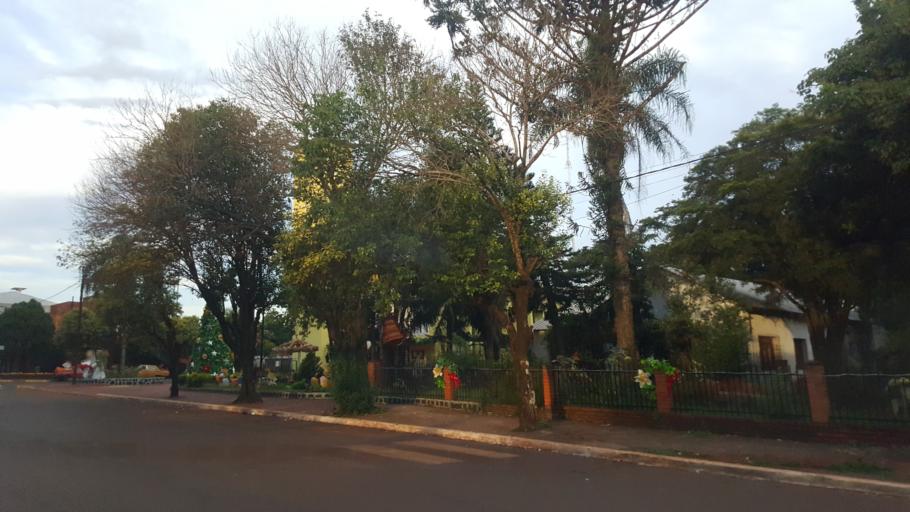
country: AR
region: Misiones
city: Jardin America
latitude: -27.0437
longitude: -55.2264
